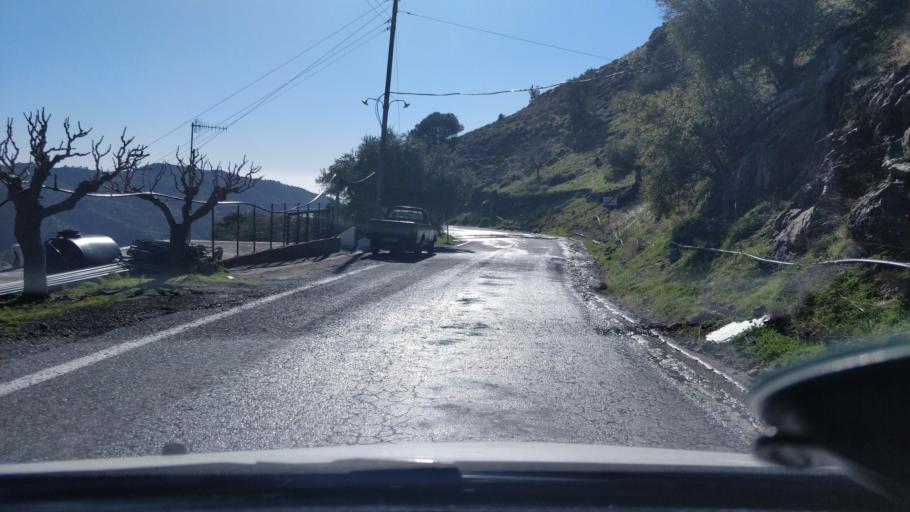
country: GR
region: Crete
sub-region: Nomos Irakleiou
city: Kastelli
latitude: 35.0390
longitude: 25.4445
